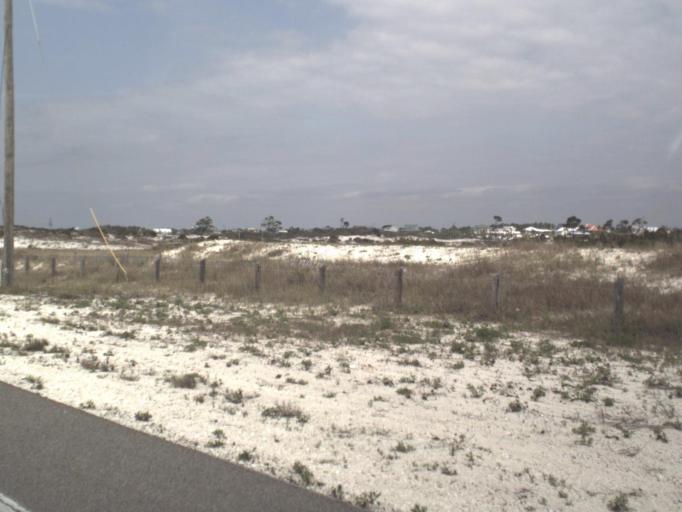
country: US
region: Alabama
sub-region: Baldwin County
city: Orange Beach
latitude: 30.2887
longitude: -87.4820
